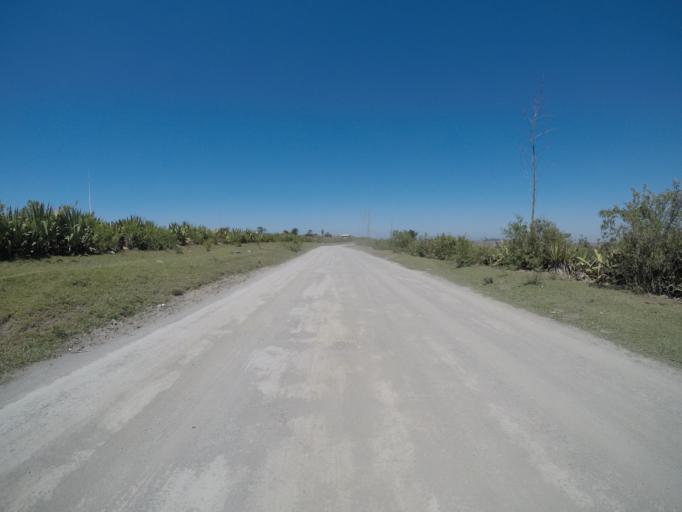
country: ZA
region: Eastern Cape
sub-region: OR Tambo District Municipality
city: Libode
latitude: -32.0062
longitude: 29.0734
